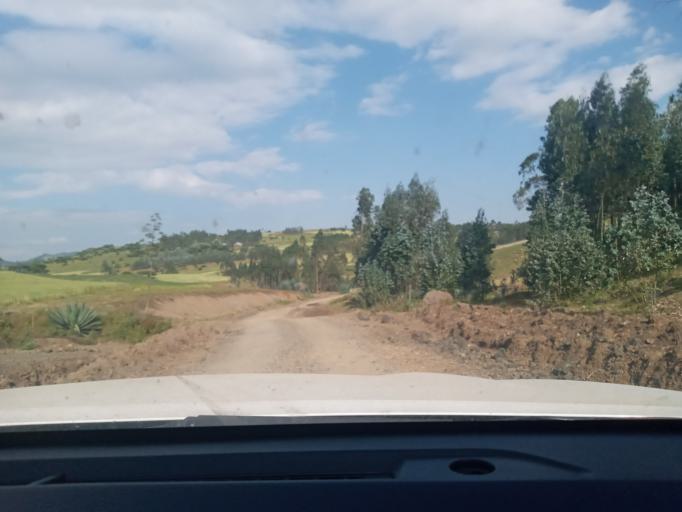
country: ET
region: Amhara
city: Were Ilu
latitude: 10.6141
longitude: 39.0445
